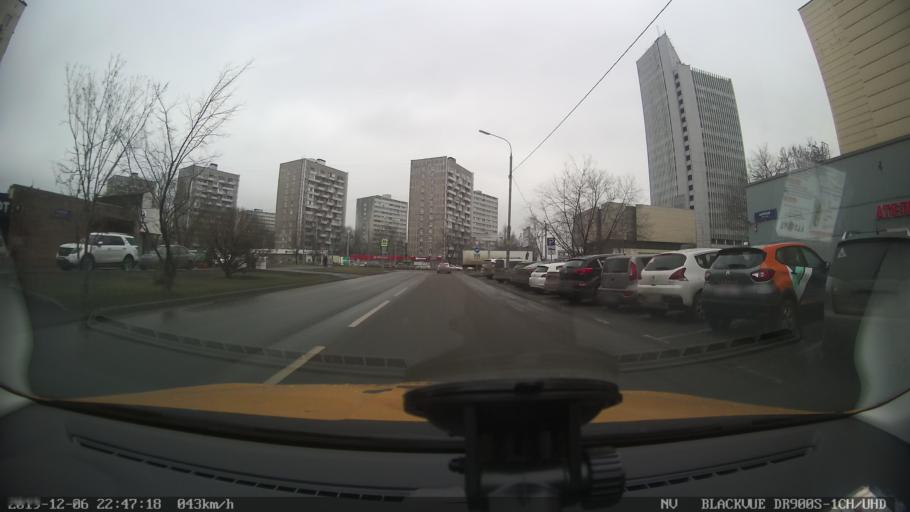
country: RU
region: Moscow
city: Metrogorodok
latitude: 55.8051
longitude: 37.7585
